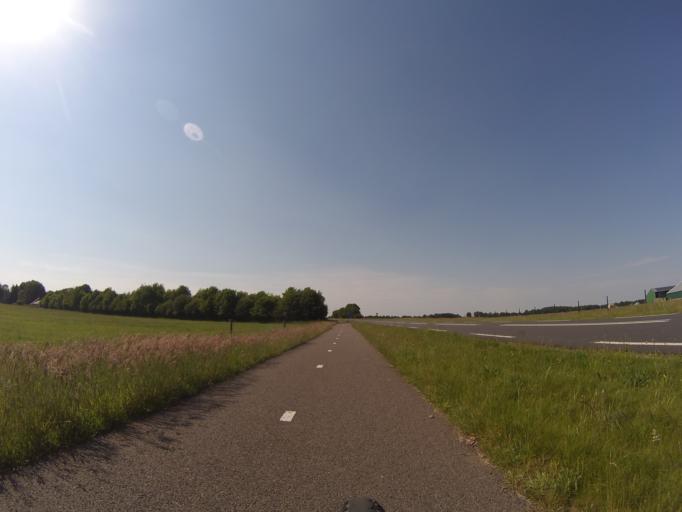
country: NL
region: Drenthe
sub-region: Gemeente Coevorden
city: Sleen
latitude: 52.7455
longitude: 6.8263
